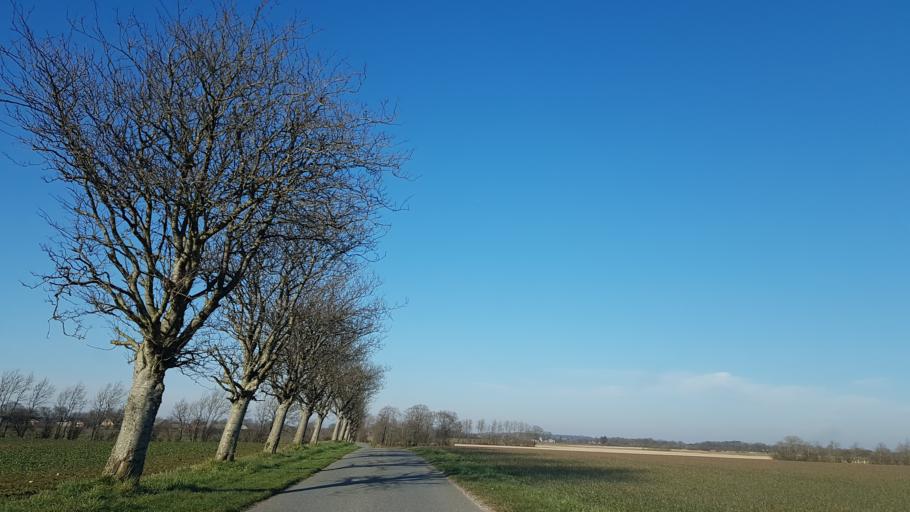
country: DK
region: South Denmark
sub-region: Kolding Kommune
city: Vamdrup
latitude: 55.4231
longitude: 9.2220
